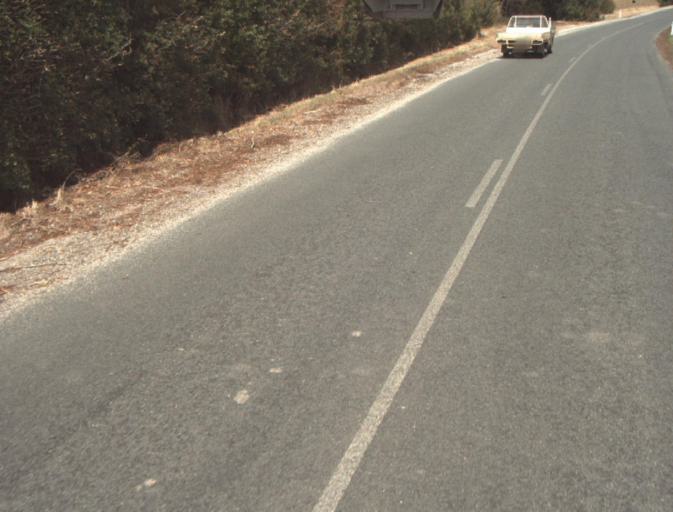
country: AU
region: Tasmania
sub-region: Launceston
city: Mayfield
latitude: -41.2308
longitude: 147.1244
